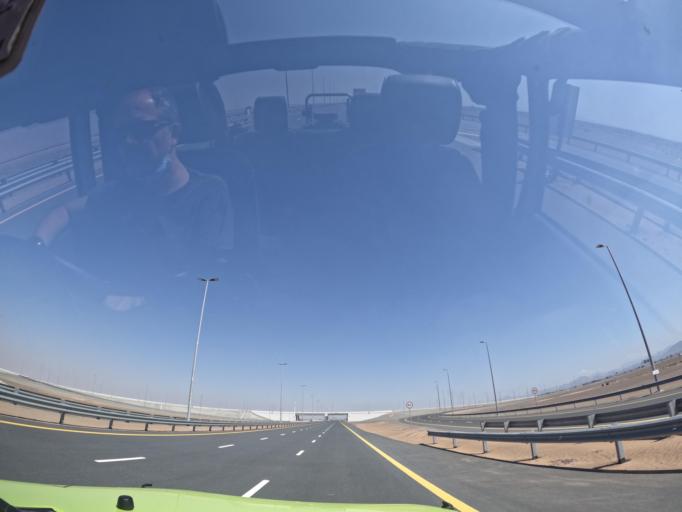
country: AE
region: Ash Shariqah
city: Adh Dhayd
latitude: 25.0694
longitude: 55.9078
